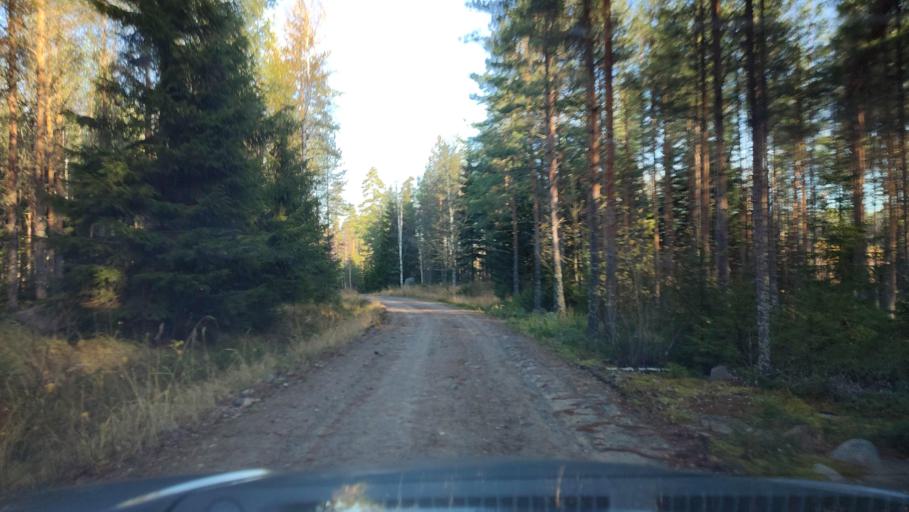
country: FI
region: Southern Ostrobothnia
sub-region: Suupohja
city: Karijoki
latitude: 62.2148
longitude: 21.6277
